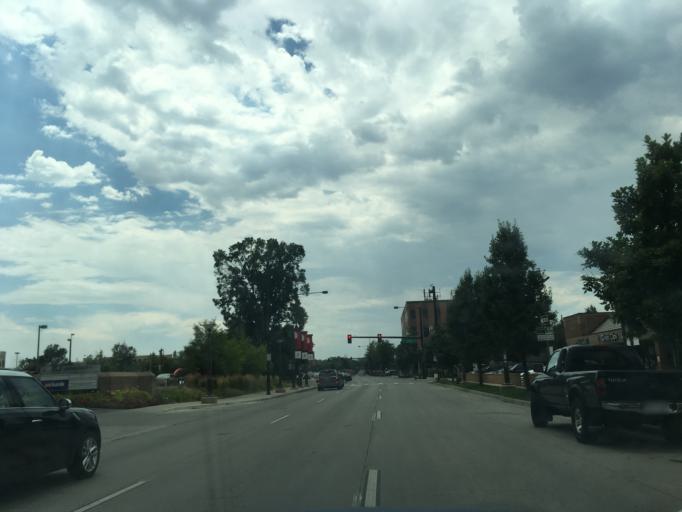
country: US
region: Colorado
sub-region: Arapahoe County
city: Glendale
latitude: 39.7201
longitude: -104.9595
